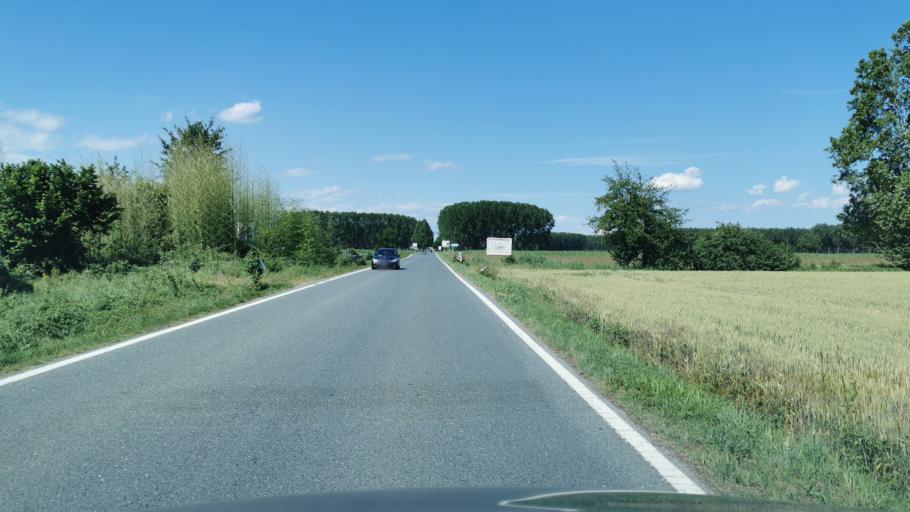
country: IT
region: Piedmont
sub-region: Provincia di Torino
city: Airasca
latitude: 44.9246
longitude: 7.4955
